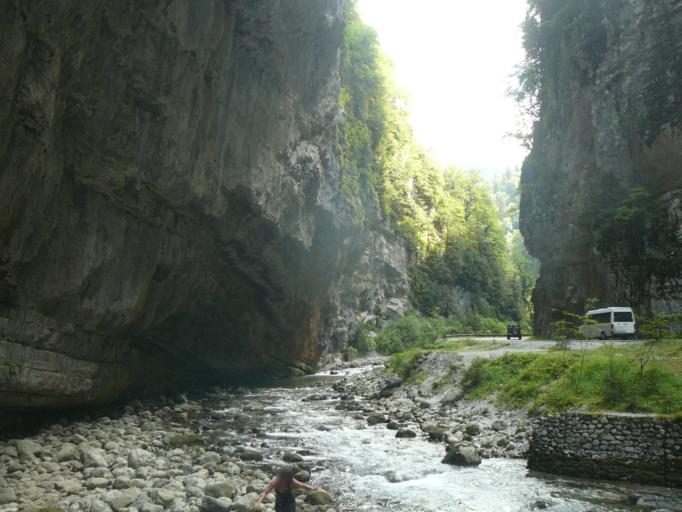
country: GE
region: Abkhazia
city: Gagra
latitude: 43.4245
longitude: 40.5194
